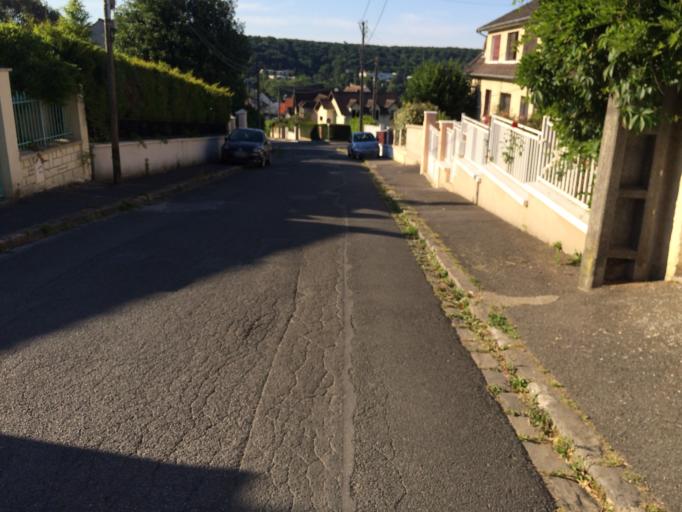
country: FR
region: Ile-de-France
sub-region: Departement de l'Essonne
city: Igny
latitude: 48.7291
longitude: 2.2198
